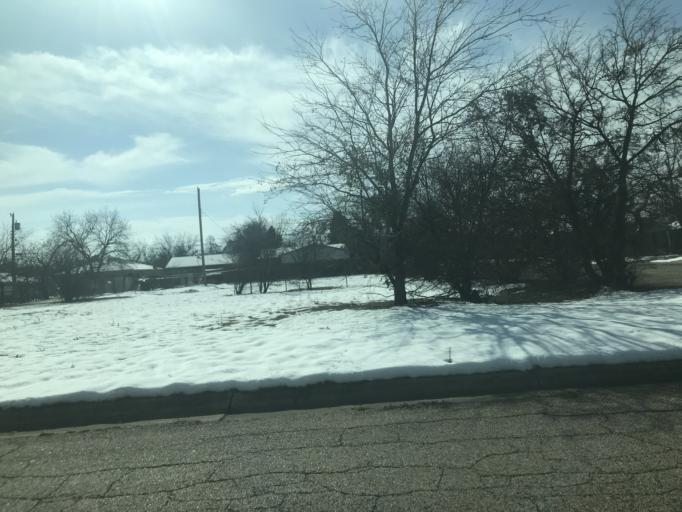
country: US
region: Texas
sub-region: Taylor County
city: Abilene
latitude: 32.4681
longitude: -99.7389
